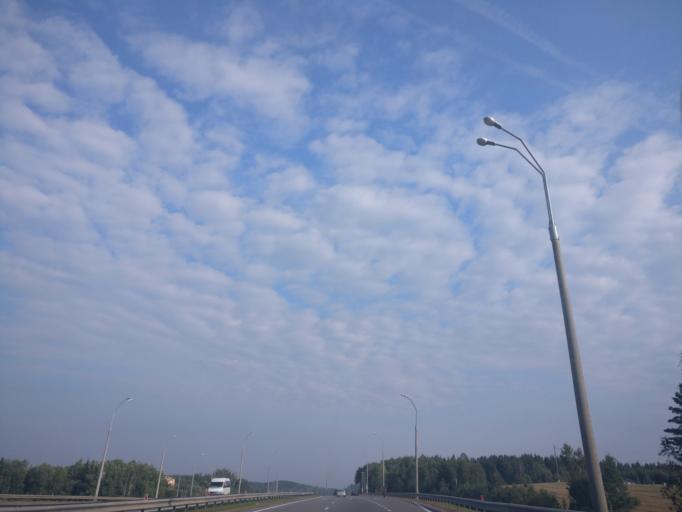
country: BY
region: Minsk
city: Lahoysk
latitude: 54.1729
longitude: 27.8198
